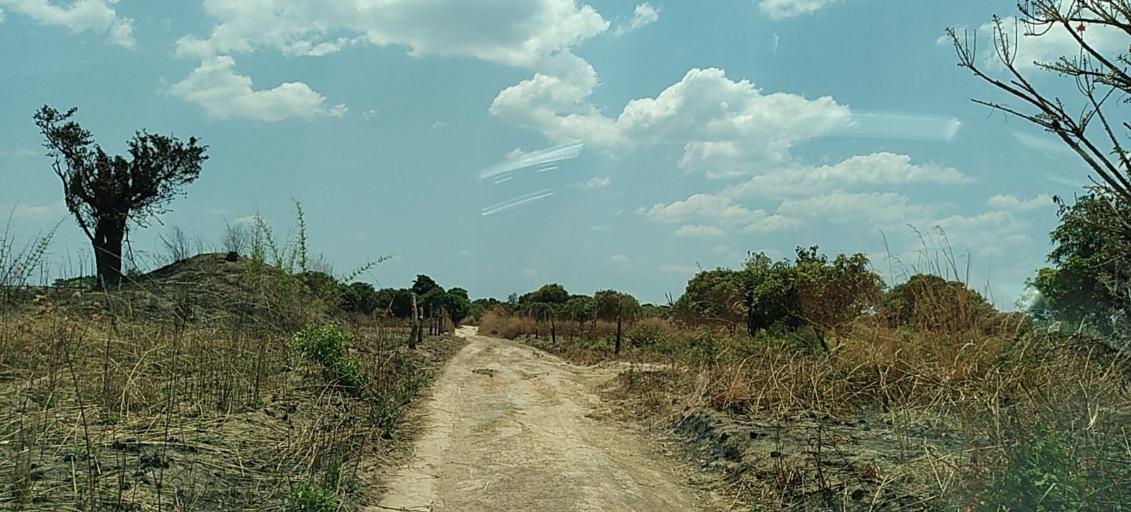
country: ZM
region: Copperbelt
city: Chililabombwe
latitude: -12.4869
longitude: 27.6677
